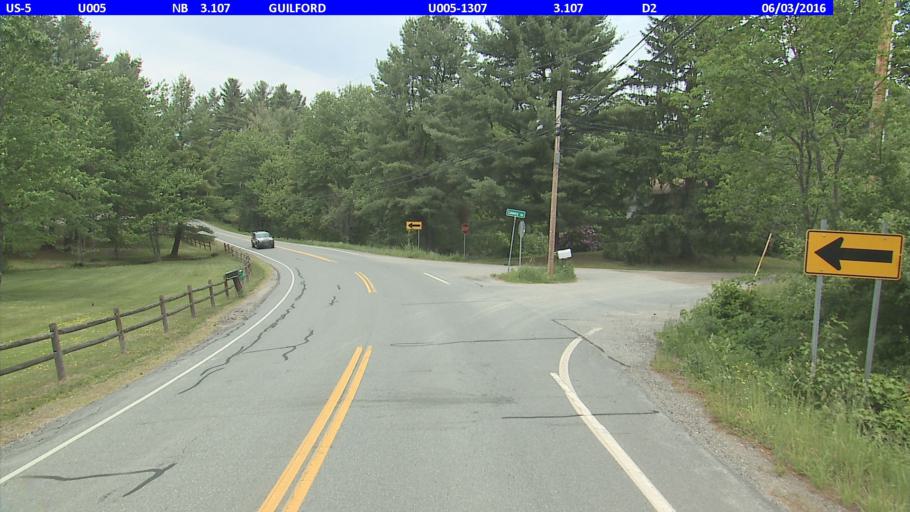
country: US
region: Vermont
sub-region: Windham County
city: Brattleboro
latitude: 42.7741
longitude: -72.5666
